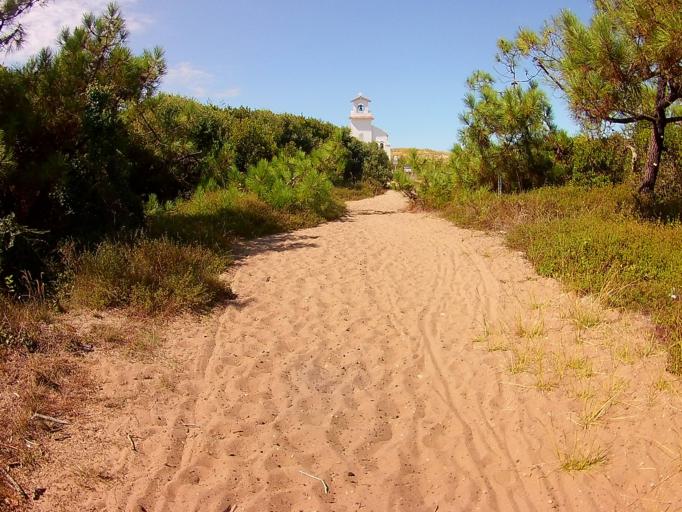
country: FR
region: Aquitaine
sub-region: Departement des Landes
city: Labenne
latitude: 43.6061
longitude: -1.4646
